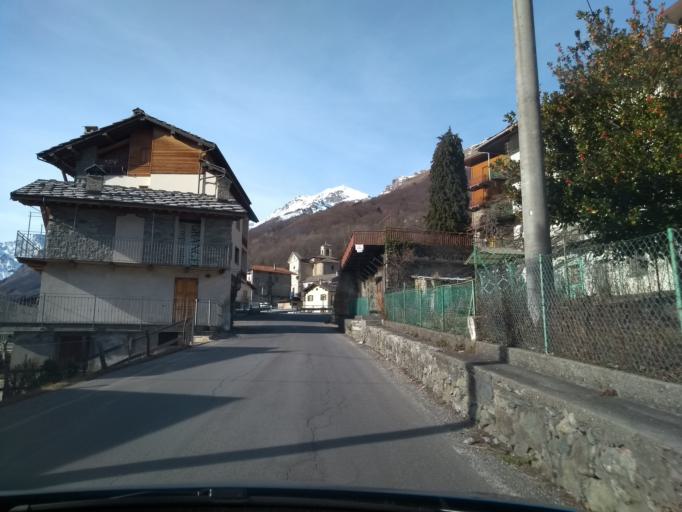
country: IT
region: Piedmont
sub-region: Provincia di Torino
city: Ala di Stura
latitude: 45.3149
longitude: 7.3073
